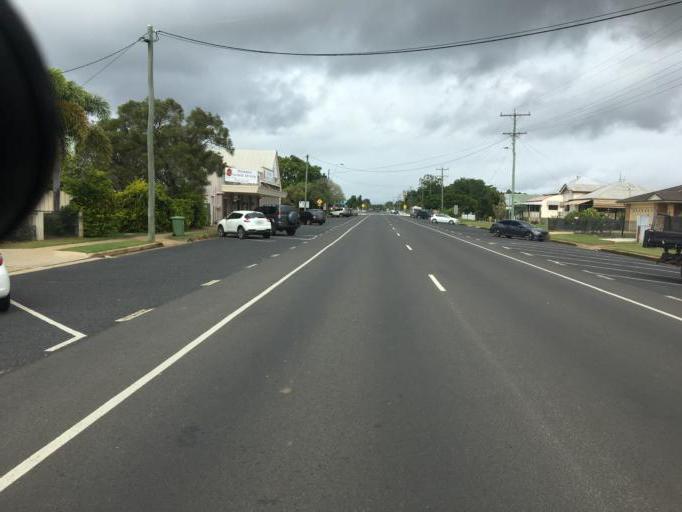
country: AU
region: Queensland
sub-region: Tablelands
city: Mareeba
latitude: -16.9931
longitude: 145.4250
